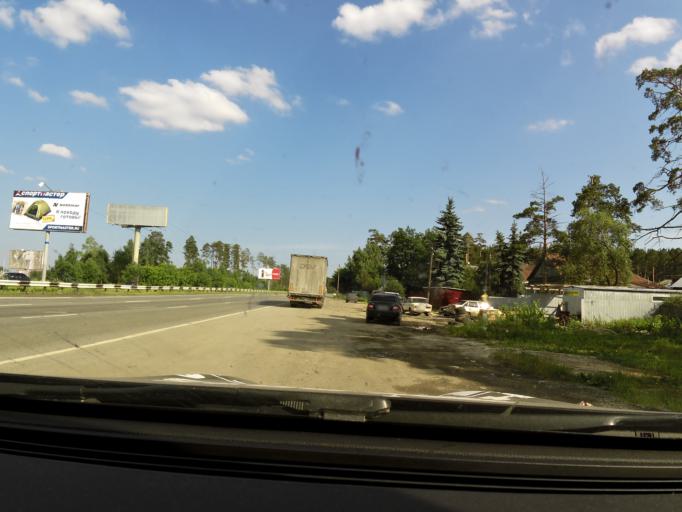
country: RU
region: Sverdlovsk
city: Shirokaya Rechka
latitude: 56.8211
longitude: 60.5011
